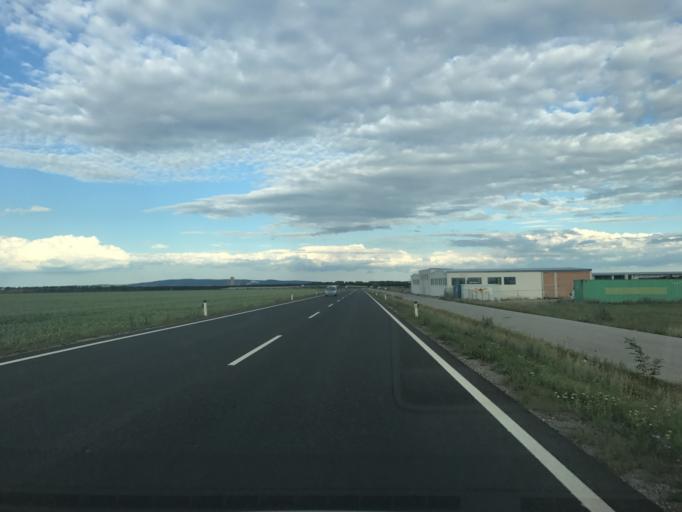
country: AT
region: Lower Austria
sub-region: Politischer Bezirk Wiener Neustadt
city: Theresienfeld
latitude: 47.8453
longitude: 16.2593
